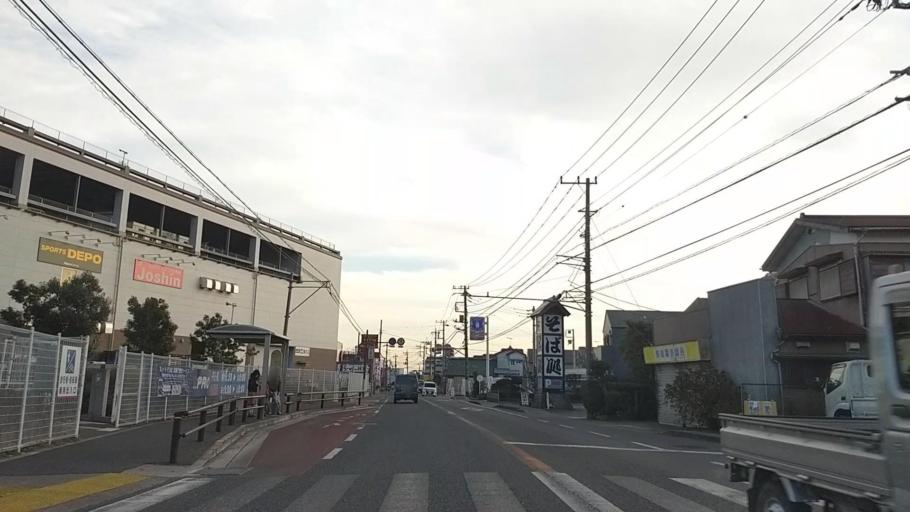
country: JP
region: Kanagawa
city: Atsugi
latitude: 35.4748
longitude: 139.3447
